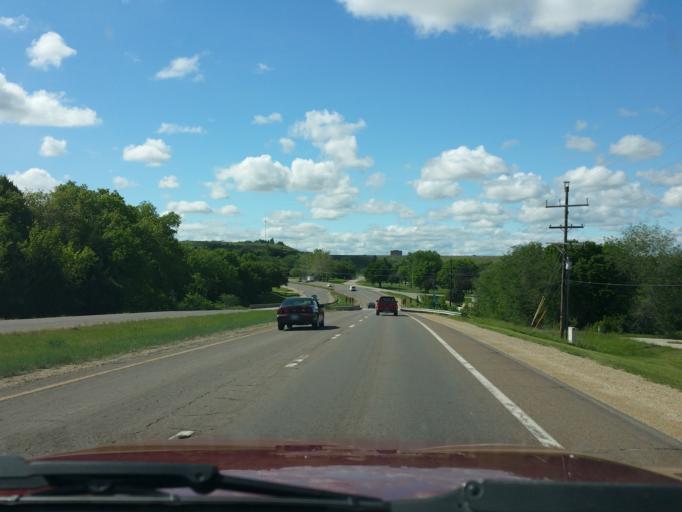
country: US
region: Kansas
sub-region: Riley County
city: Manhattan
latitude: 39.2434
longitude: -96.5940
